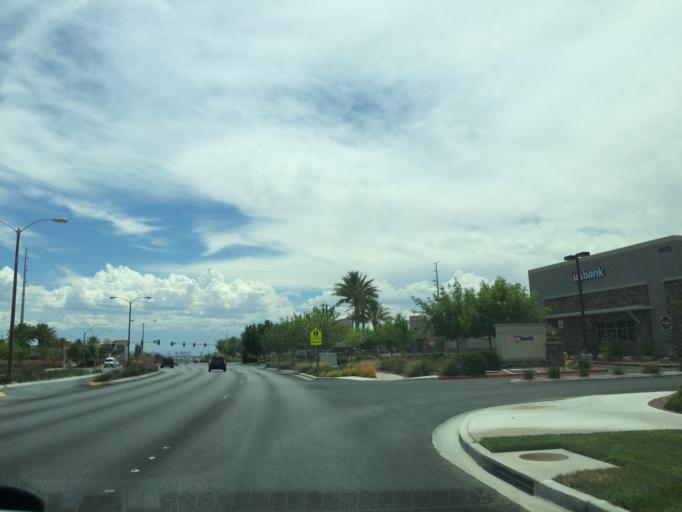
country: US
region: Nevada
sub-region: Clark County
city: North Las Vegas
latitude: 36.2782
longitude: -115.1798
